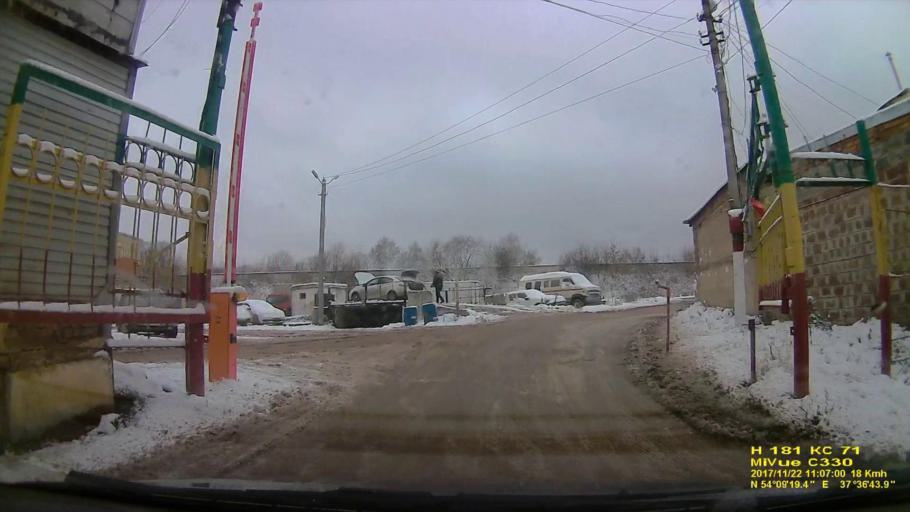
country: RU
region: Tula
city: Mendeleyevskiy
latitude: 54.1554
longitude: 37.6121
